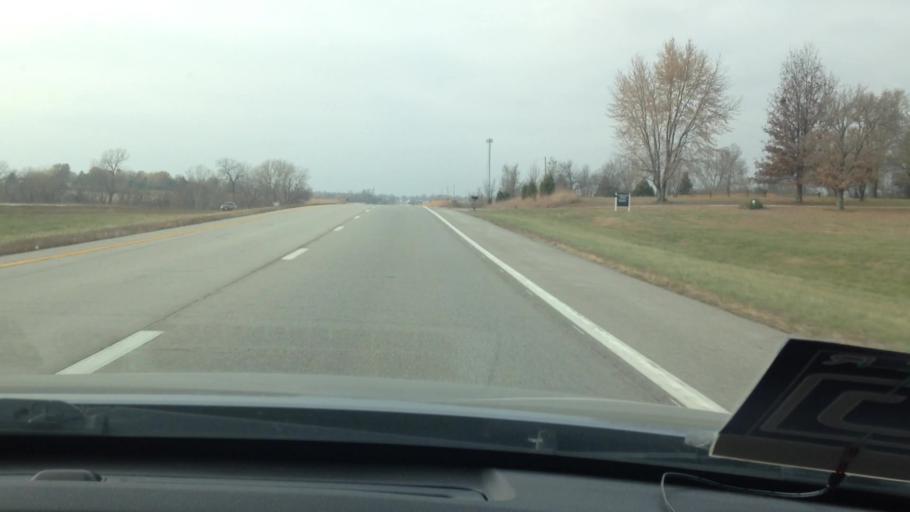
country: US
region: Missouri
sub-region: Cass County
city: Garden City
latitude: 38.5462
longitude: -94.1683
